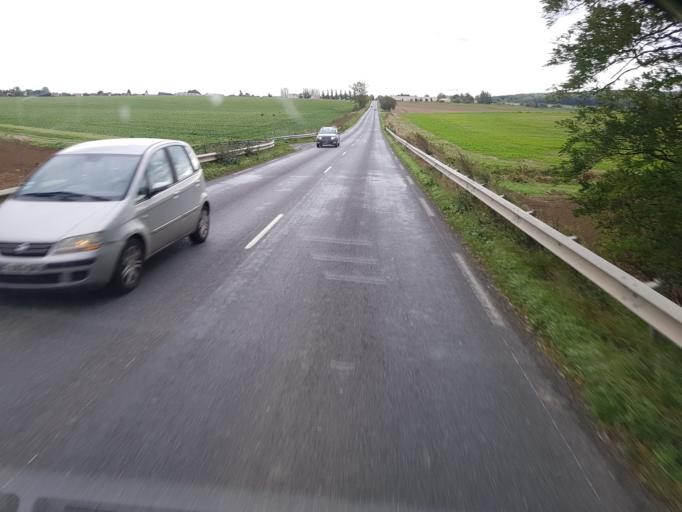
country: FR
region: Ile-de-France
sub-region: Departement de Seine-et-Marne
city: Saint-Soupplets
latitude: 49.0477
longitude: 2.7909
